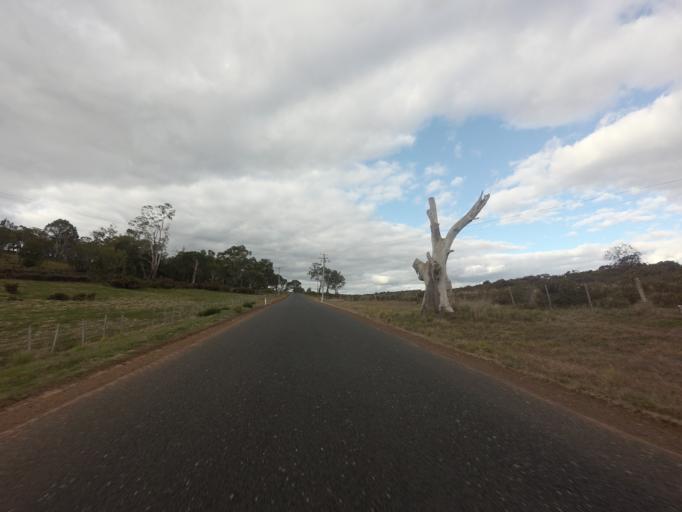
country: AU
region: Tasmania
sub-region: Northern Midlands
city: Evandale
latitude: -41.8957
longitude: 147.4087
